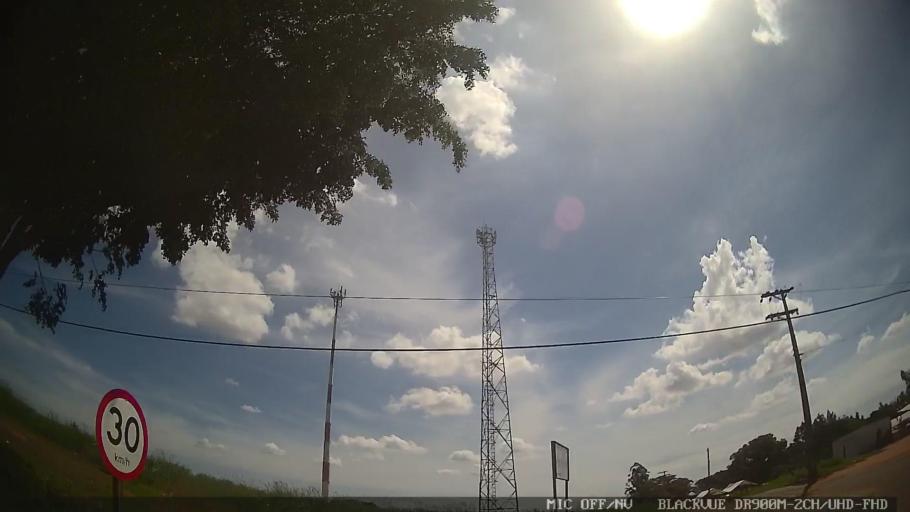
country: BR
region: Sao Paulo
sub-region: Artur Nogueira
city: Artur Nogueira
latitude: -22.6108
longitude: -47.0870
